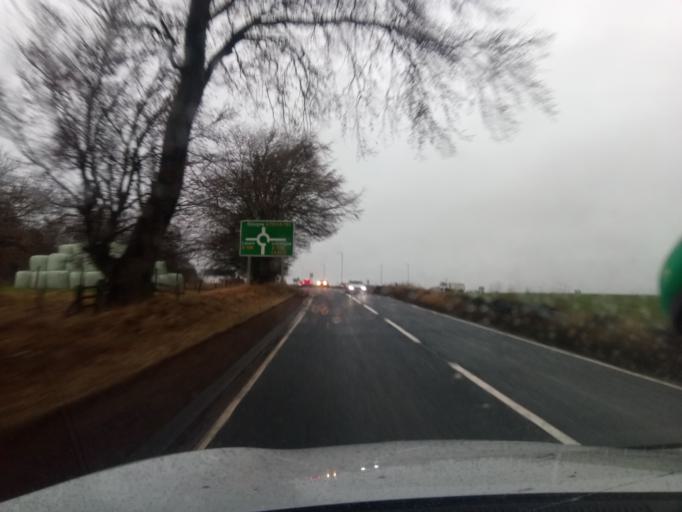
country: GB
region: Scotland
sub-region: South Lanarkshire
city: Lanark
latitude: 55.7055
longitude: -3.7230
